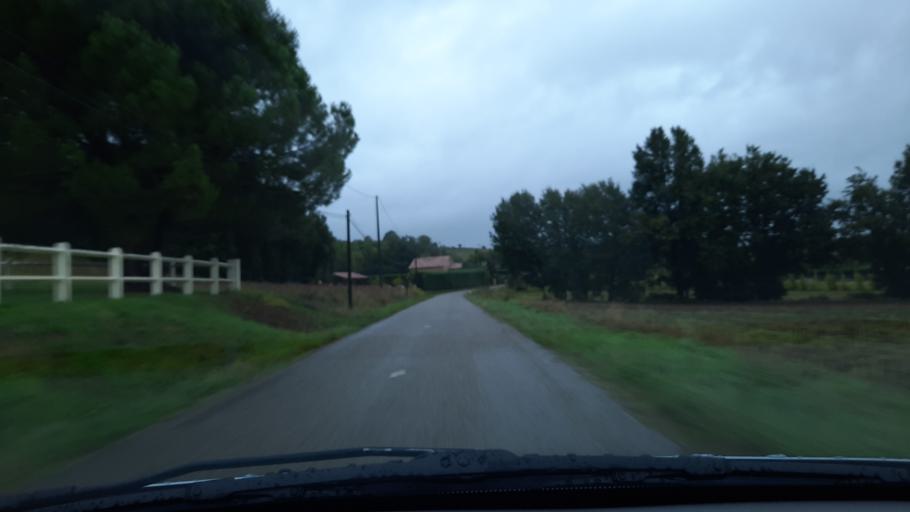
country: FR
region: Midi-Pyrenees
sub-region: Departement du Tarn-et-Garonne
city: Lafrancaise
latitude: 44.1883
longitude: 1.2776
